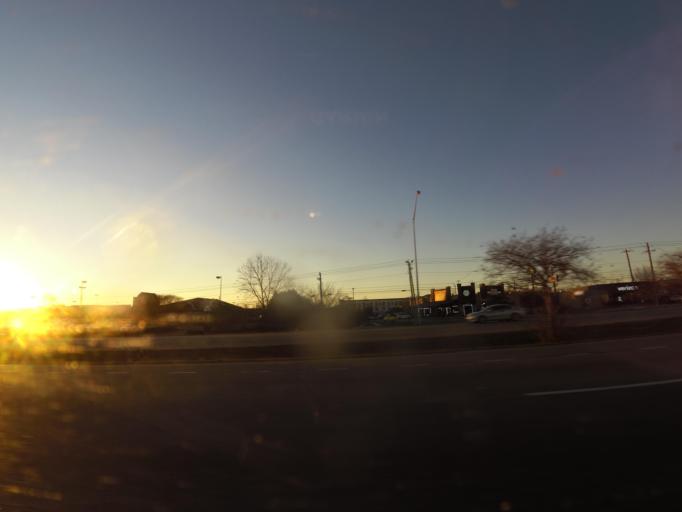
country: US
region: Alabama
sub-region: Montgomery County
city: Montgomery
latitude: 32.3524
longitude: -86.2193
